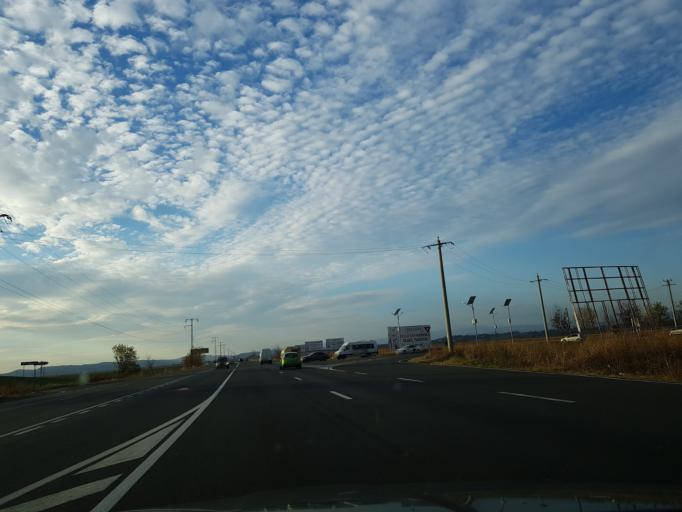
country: RO
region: Prahova
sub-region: Oras Baicoi
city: Liliesti
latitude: 45.0027
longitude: 25.8842
